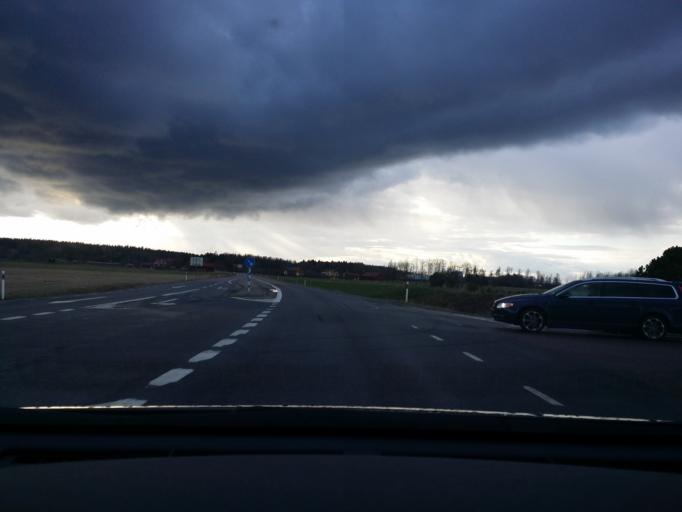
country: SE
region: Soedermanland
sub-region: Eskilstuna Kommun
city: Arla
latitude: 59.3884
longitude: 16.6471
